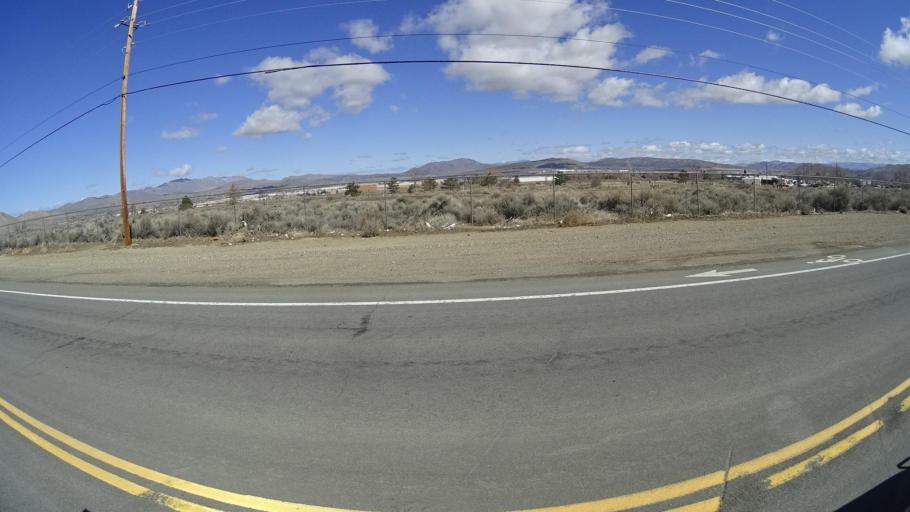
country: US
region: Nevada
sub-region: Washoe County
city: Lemmon Valley
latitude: 39.6248
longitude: -119.8870
